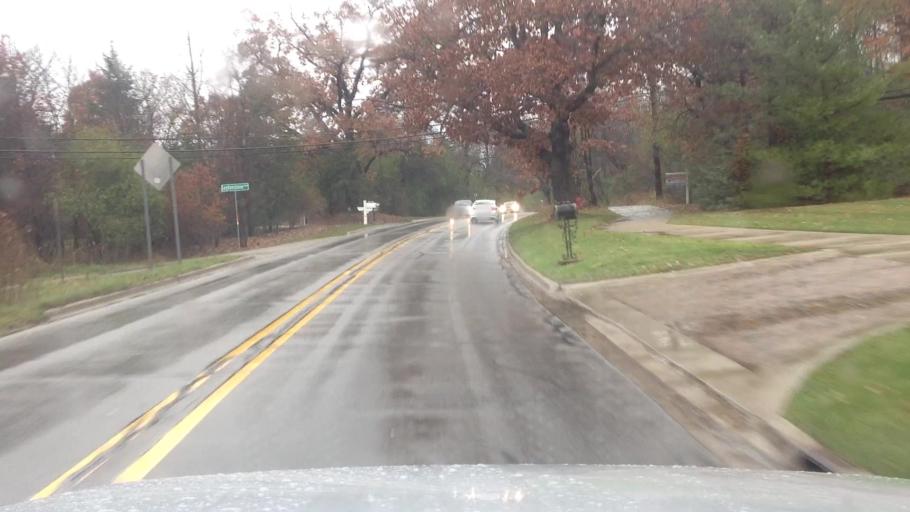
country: US
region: Michigan
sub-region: Oakland County
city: West Bloomfield Township
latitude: 42.5566
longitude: -83.4051
